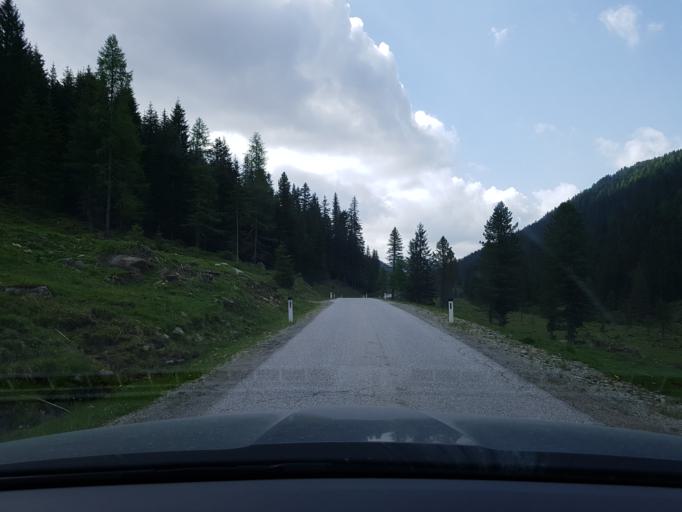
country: AT
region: Salzburg
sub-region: Politischer Bezirk Tamsweg
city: Thomatal
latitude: 47.0252
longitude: 13.7622
